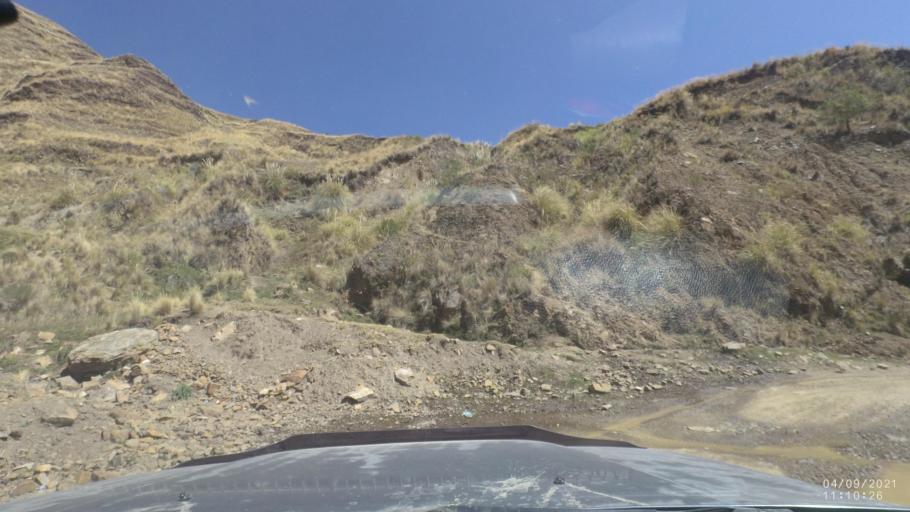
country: BO
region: Cochabamba
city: Sipe Sipe
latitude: -17.2784
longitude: -66.4822
